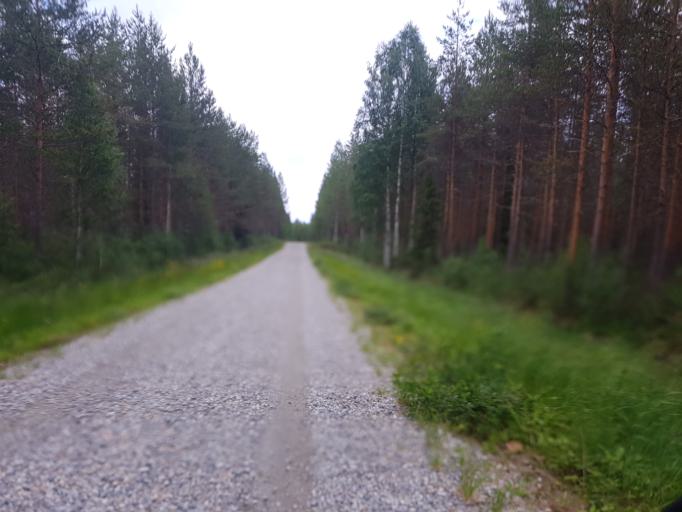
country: FI
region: Kainuu
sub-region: Kehys-Kainuu
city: Kuhmo
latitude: 64.4527
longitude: 29.6965
